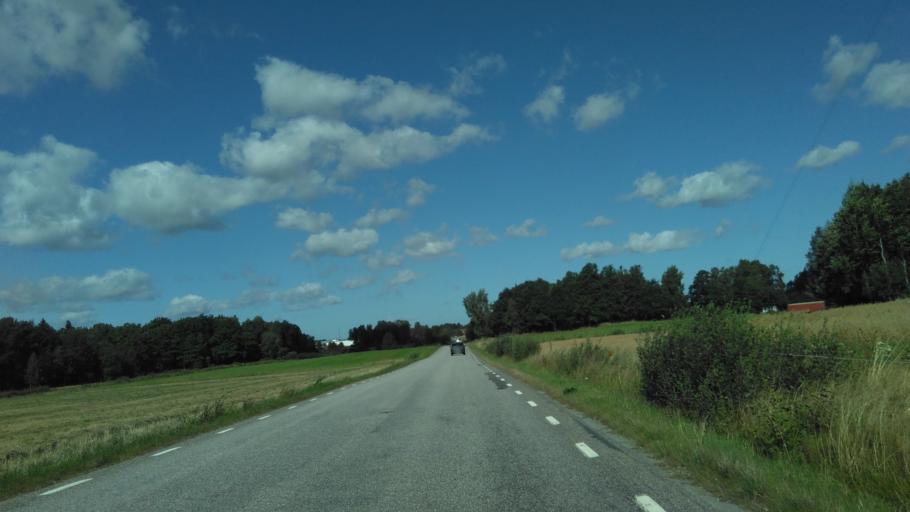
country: SE
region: Vaestra Goetaland
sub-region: Herrljunga Kommun
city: Herrljunga
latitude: 58.1574
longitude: 13.0107
